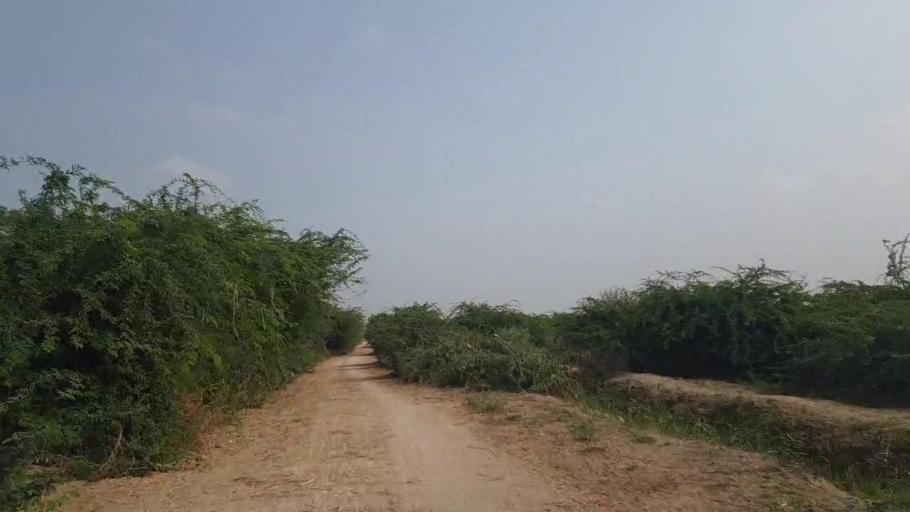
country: PK
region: Sindh
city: Badin
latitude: 24.5475
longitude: 68.7075
